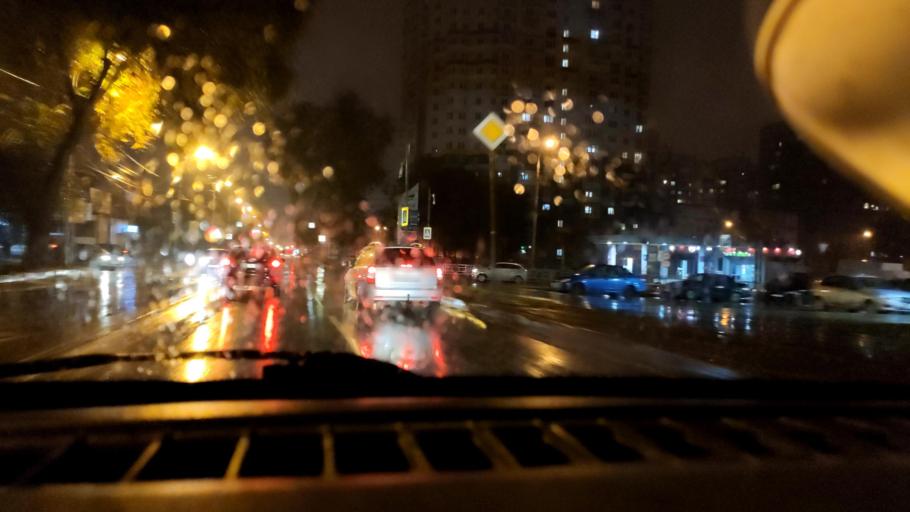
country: RU
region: Samara
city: Samara
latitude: 53.1938
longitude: 50.1389
